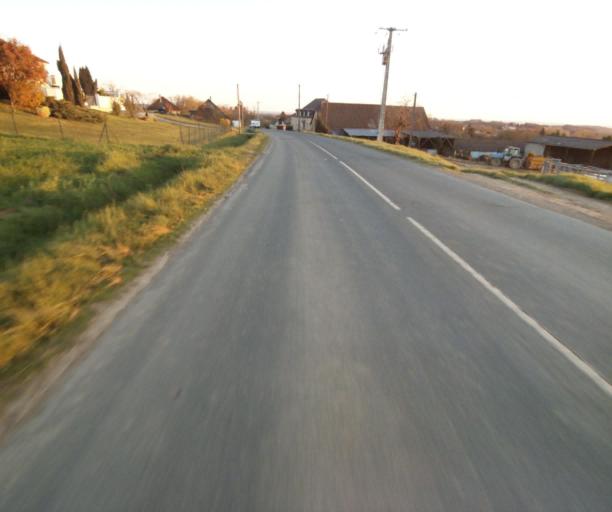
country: FR
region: Limousin
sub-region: Departement de la Correze
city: Sainte-Fereole
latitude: 45.2759
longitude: 1.5627
